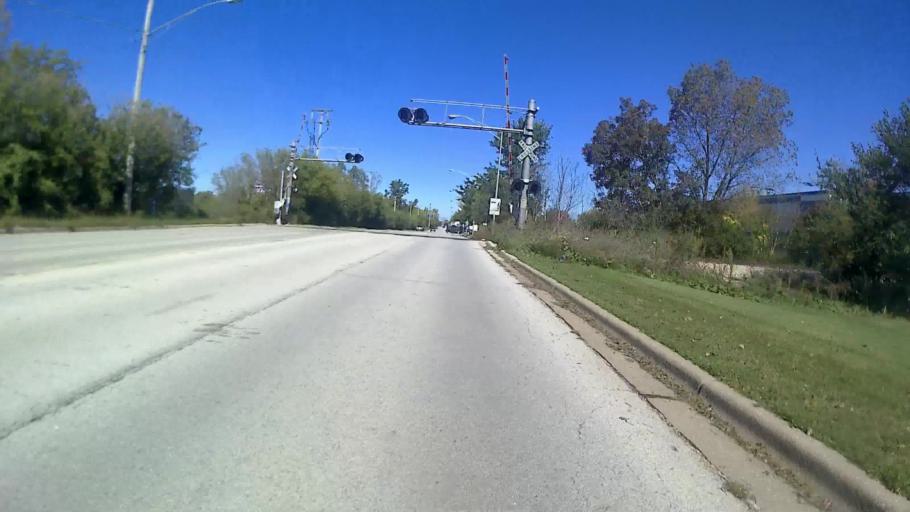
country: US
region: Illinois
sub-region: DuPage County
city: Villa Park
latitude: 41.9097
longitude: -88.0078
